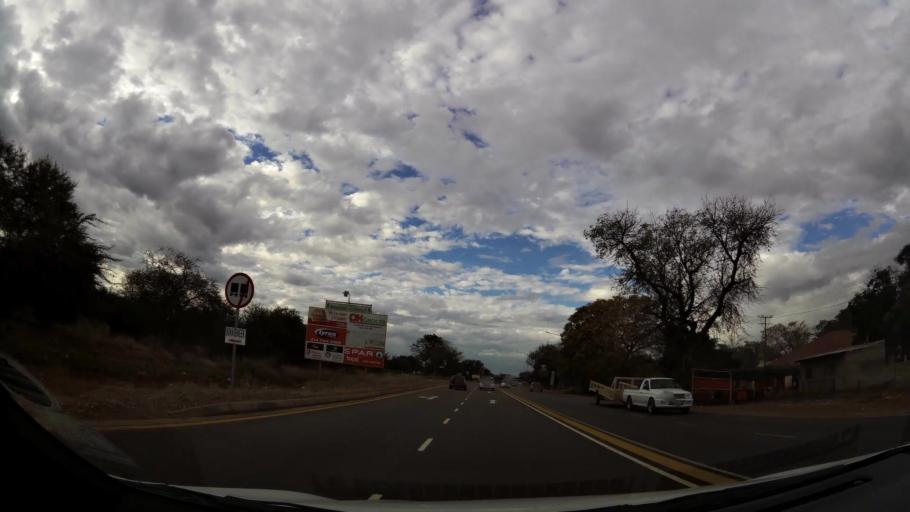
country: ZA
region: Limpopo
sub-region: Waterberg District Municipality
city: Modimolle
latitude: -24.5269
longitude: 28.7068
